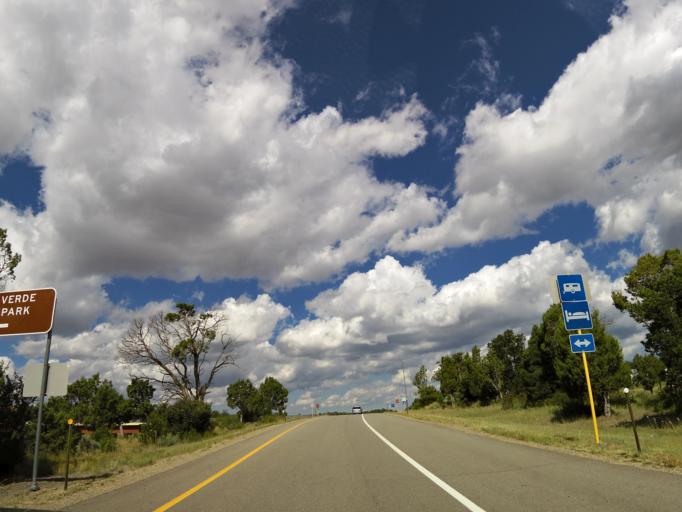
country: US
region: Colorado
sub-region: Montezuma County
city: Mancos
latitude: 37.3405
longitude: -108.4098
